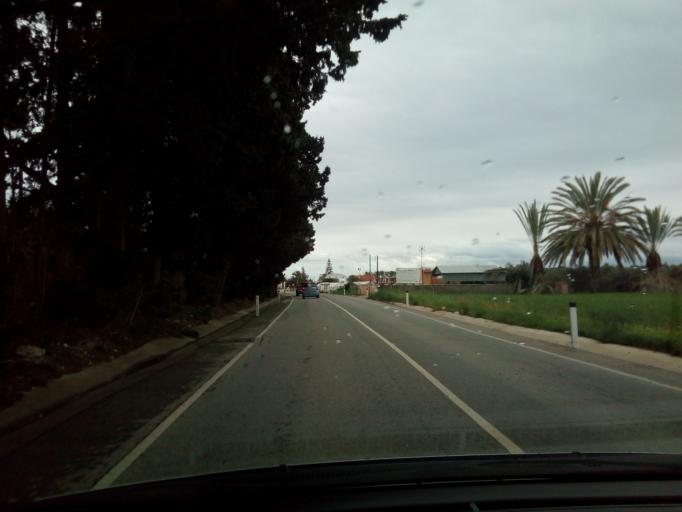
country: CY
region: Larnaka
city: Kofinou
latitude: 34.7439
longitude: 33.3235
